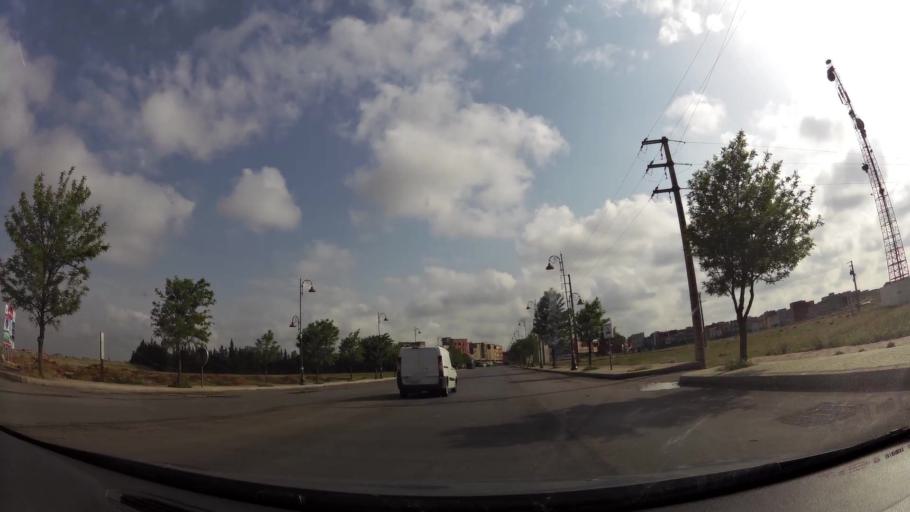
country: MA
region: Rabat-Sale-Zemmour-Zaer
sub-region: Khemisset
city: Tiflet
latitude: 33.8825
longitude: -6.3217
